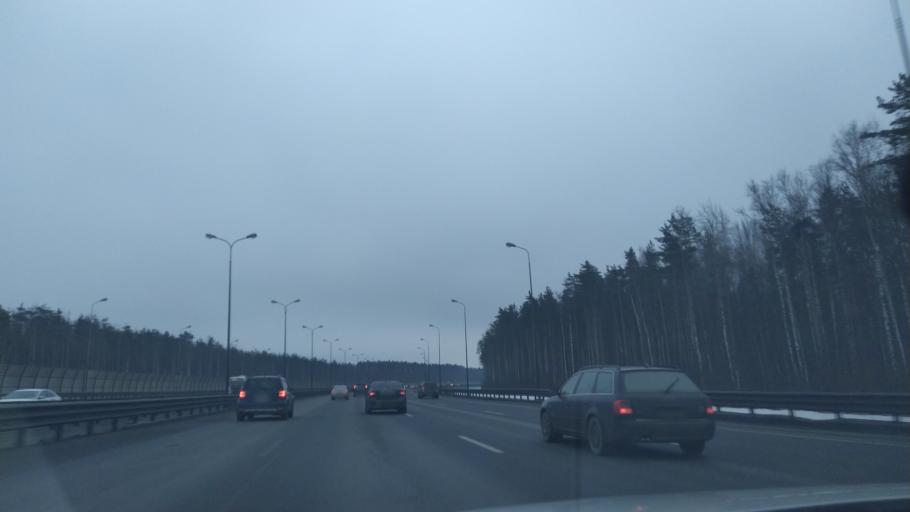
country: RU
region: St.-Petersburg
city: Krasnogvargeisky
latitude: 59.9744
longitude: 30.5406
